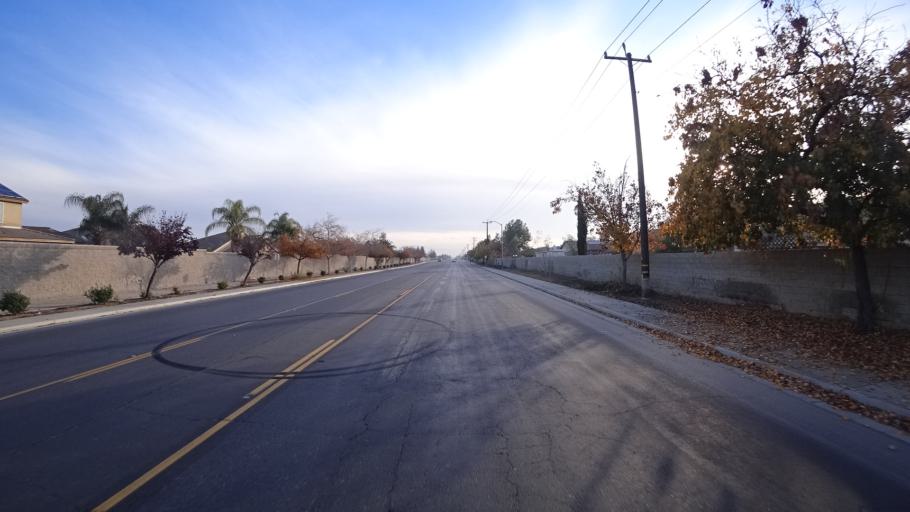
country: US
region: California
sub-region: Kern County
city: Rosedale
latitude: 35.4051
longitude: -119.1407
